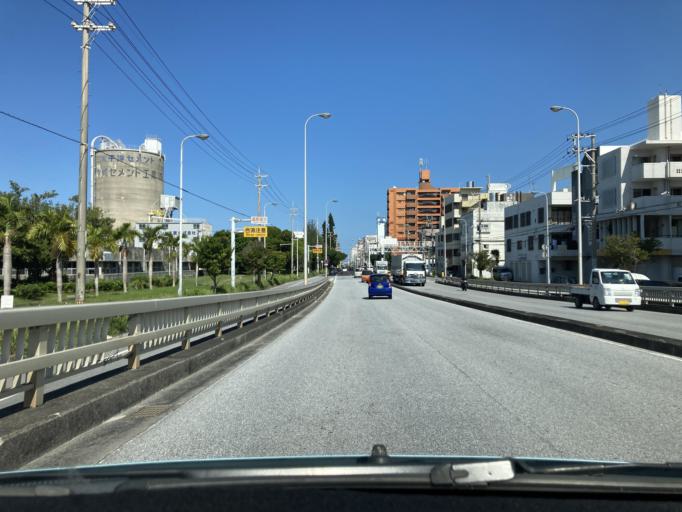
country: JP
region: Okinawa
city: Naha-shi
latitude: 26.2314
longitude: 127.6816
